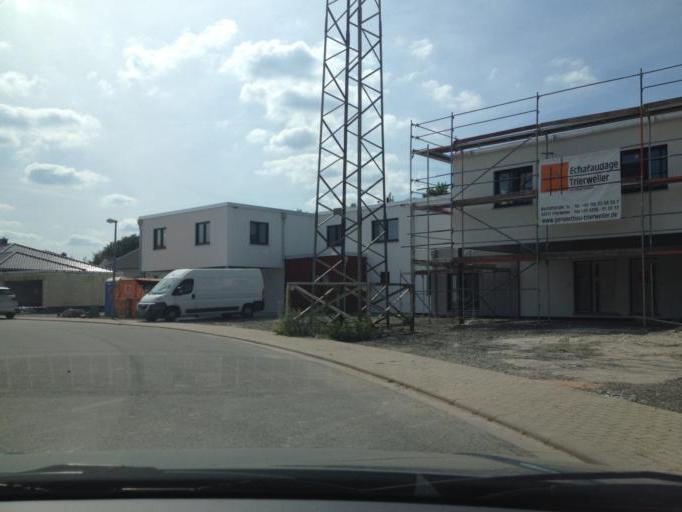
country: DE
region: Saarland
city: Neunkirchen
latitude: 49.3363
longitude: 7.1731
